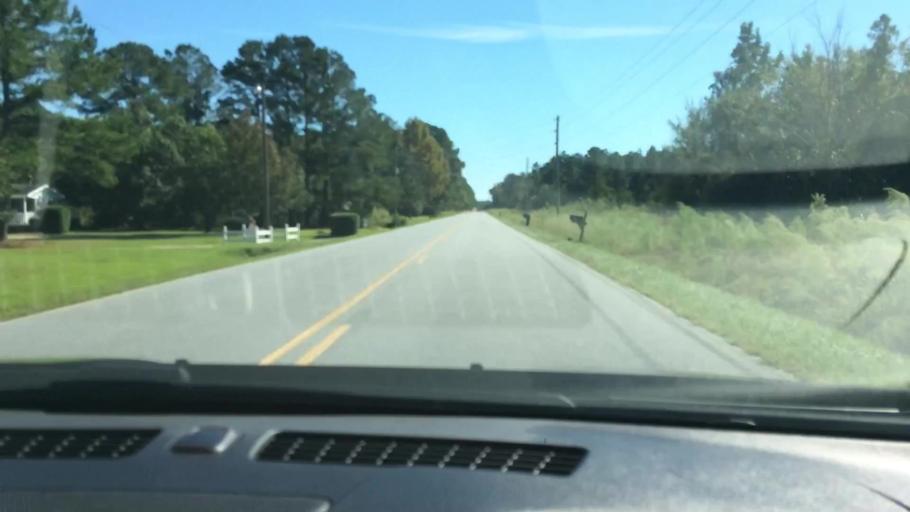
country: US
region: North Carolina
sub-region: Pitt County
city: Grifton
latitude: 35.4005
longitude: -77.4090
